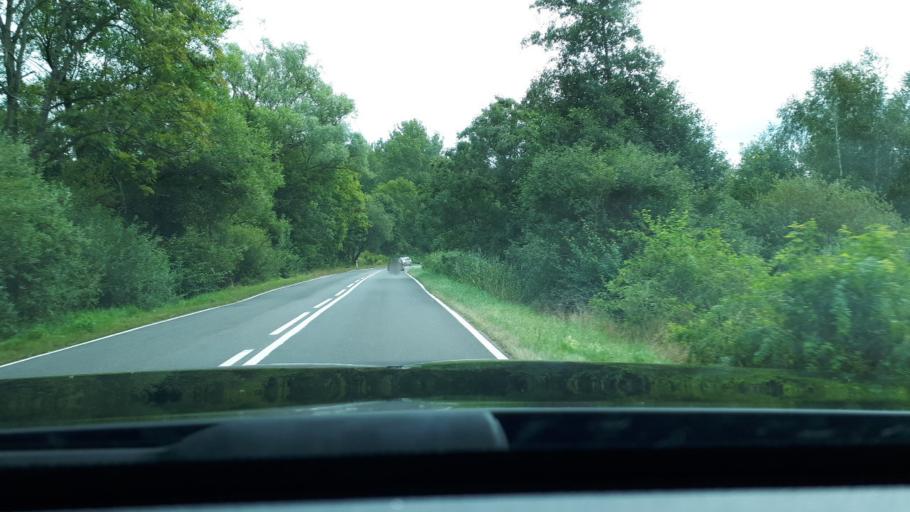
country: PL
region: Lower Silesian Voivodeship
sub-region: Powiat lwowecki
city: Lwowek Slaski
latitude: 51.1003
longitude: 15.5267
